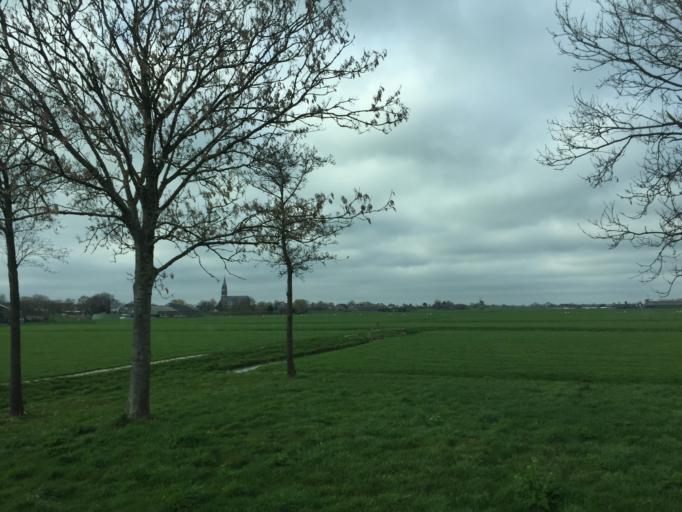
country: NL
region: South Holland
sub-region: Gemeente Kaag en Braassem
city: Oude Wetering
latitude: 52.1878
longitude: 4.5919
